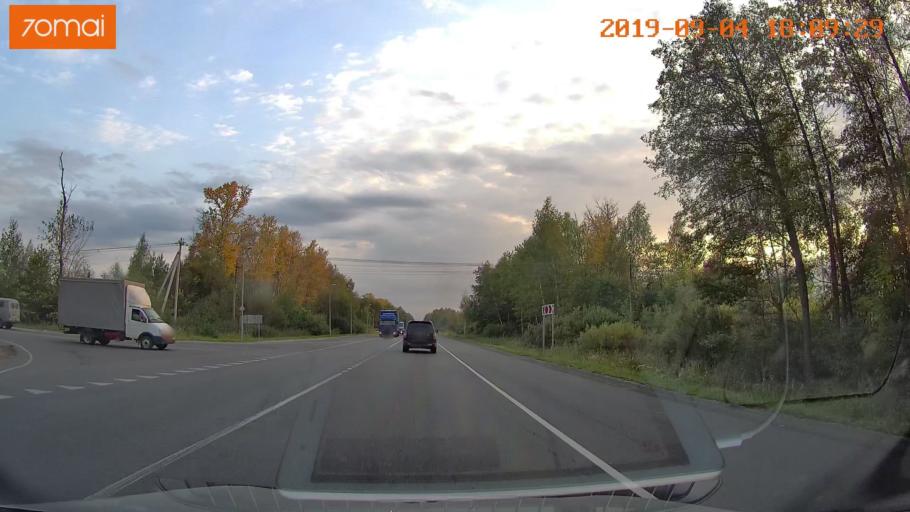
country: RU
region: Moskovskaya
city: Khorlovo
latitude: 55.3969
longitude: 38.7757
